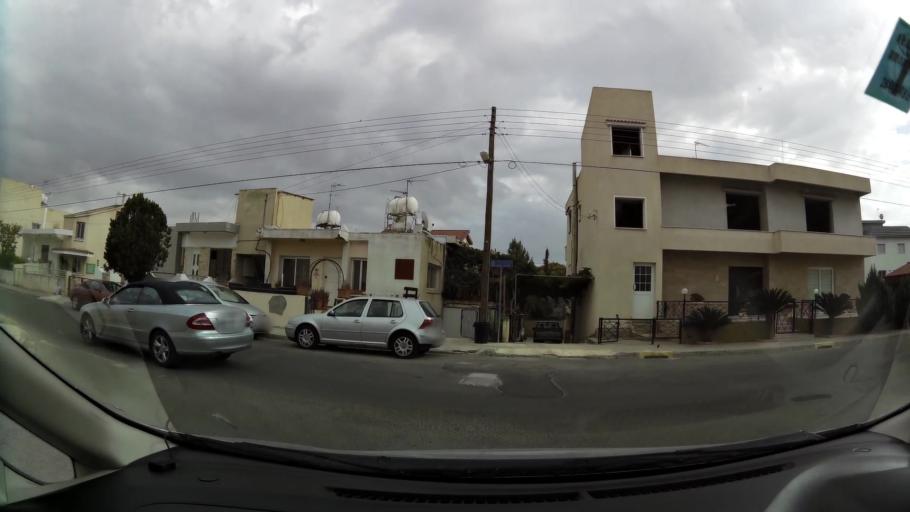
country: CY
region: Lefkosia
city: Geri
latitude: 35.1093
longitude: 33.3881
